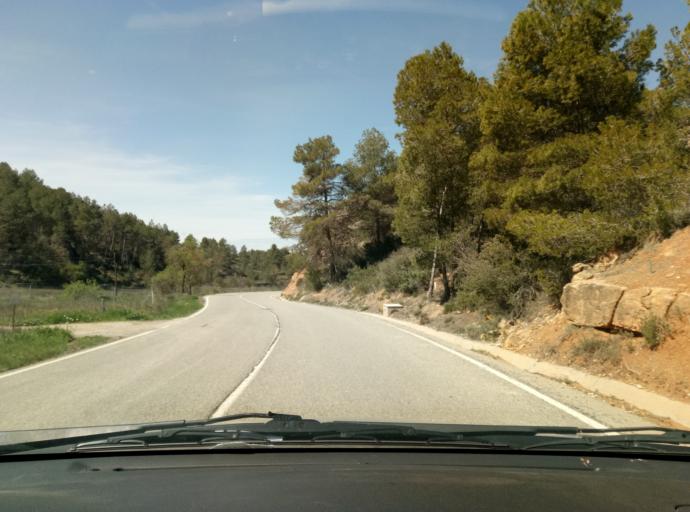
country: ES
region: Catalonia
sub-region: Provincia de Tarragona
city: Ulldemolins
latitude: 41.4259
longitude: 0.8789
